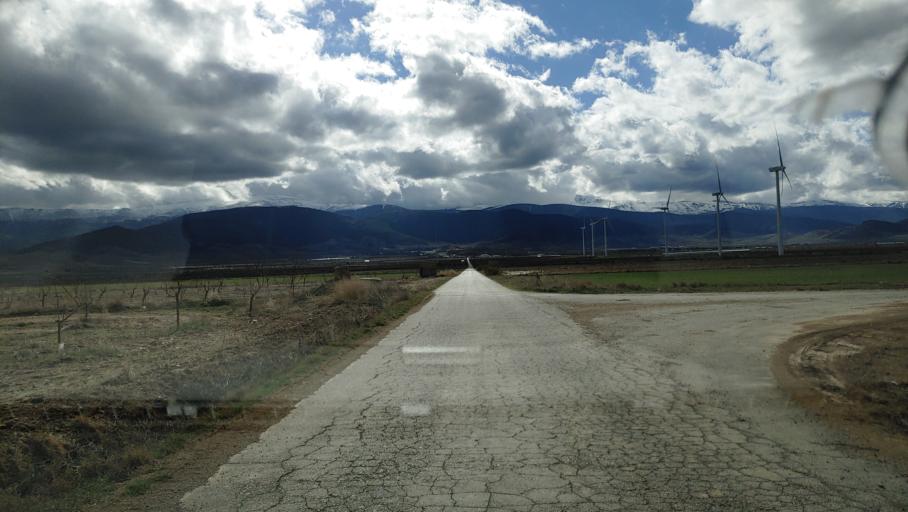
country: ES
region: Andalusia
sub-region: Provincia de Granada
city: Hueneja
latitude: 37.2161
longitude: -2.9713
